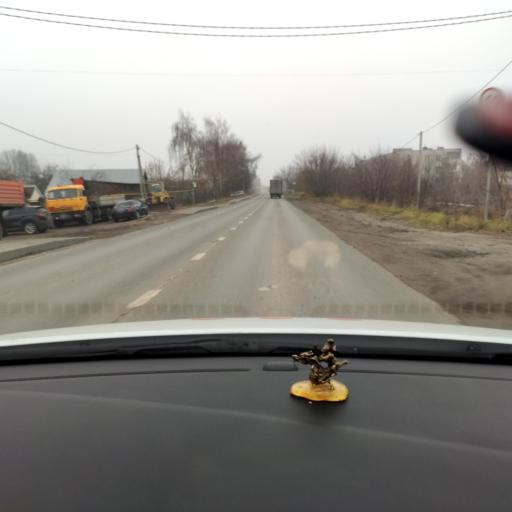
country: RU
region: Tatarstan
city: Osinovo
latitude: 55.8576
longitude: 48.8886
